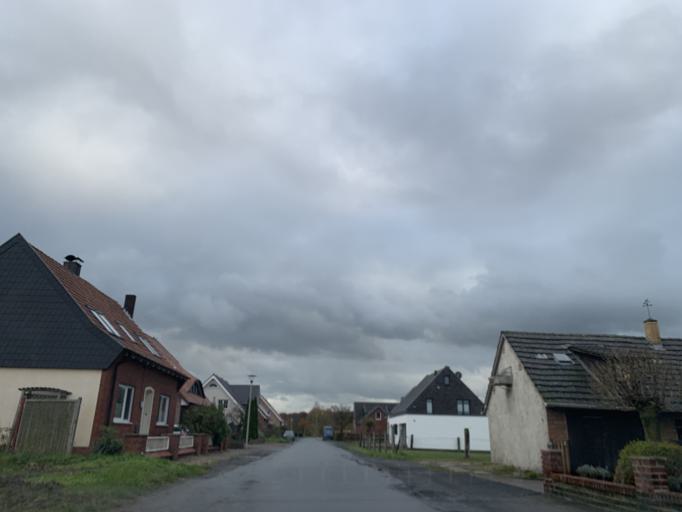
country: DE
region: North Rhine-Westphalia
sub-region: Regierungsbezirk Munster
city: Steinfurt
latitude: 52.1145
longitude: 7.3806
